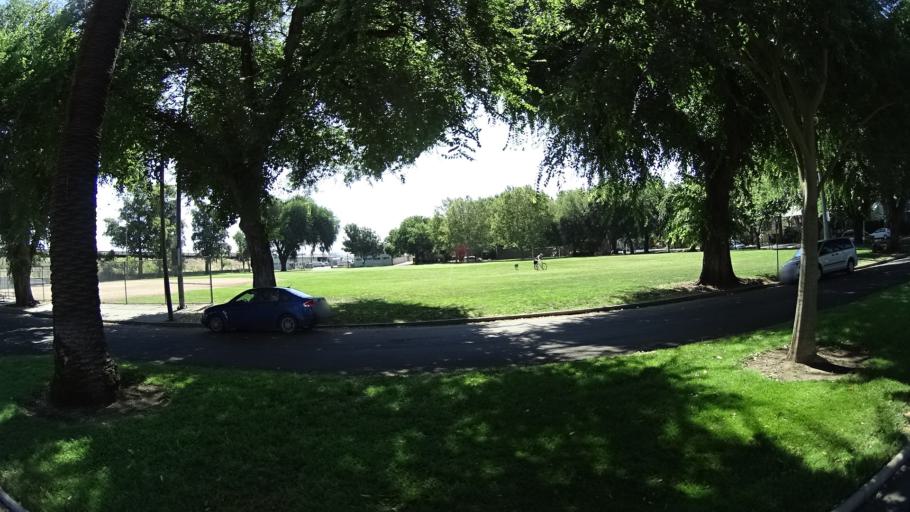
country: US
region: California
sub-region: Sacramento County
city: Sacramento
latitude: 38.5844
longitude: -121.4751
